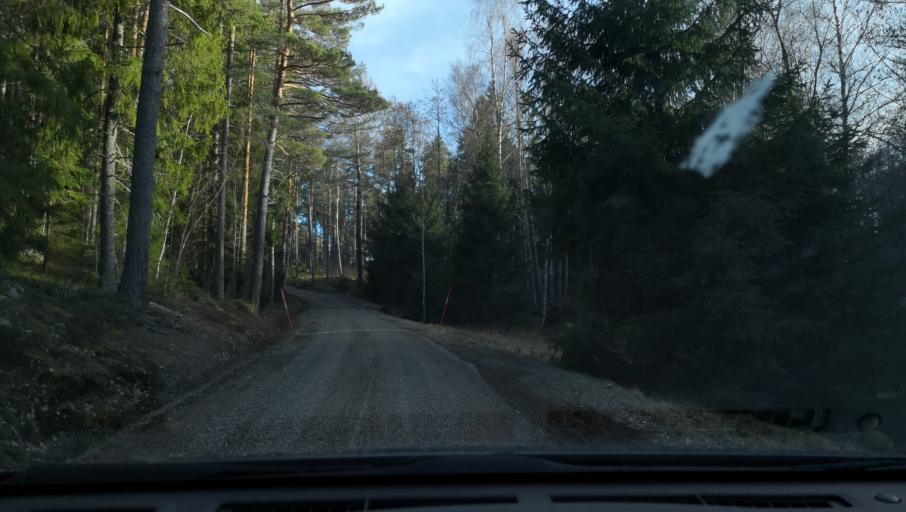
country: SE
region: Vaestmanland
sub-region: Arboga Kommun
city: Arboga
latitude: 59.4360
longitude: 15.7515
